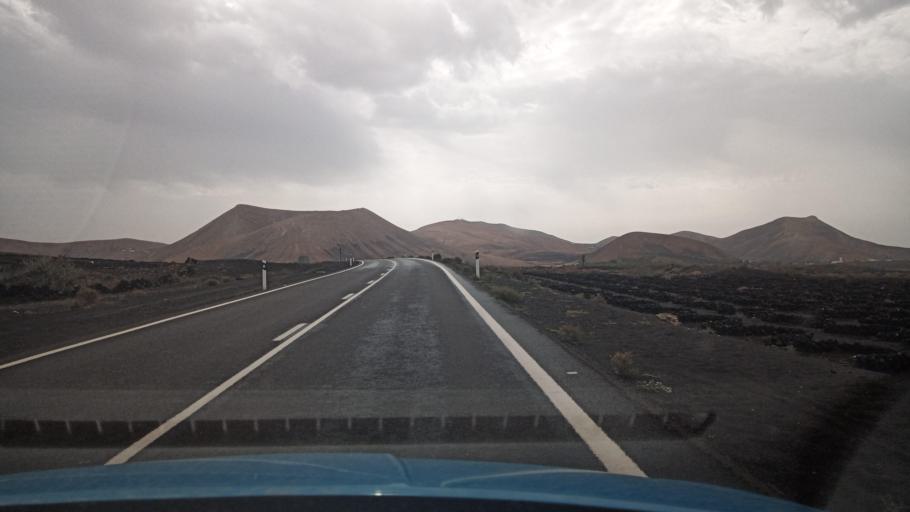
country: ES
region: Canary Islands
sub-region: Provincia de Las Palmas
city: Yaiza
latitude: 28.9552
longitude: -13.7356
